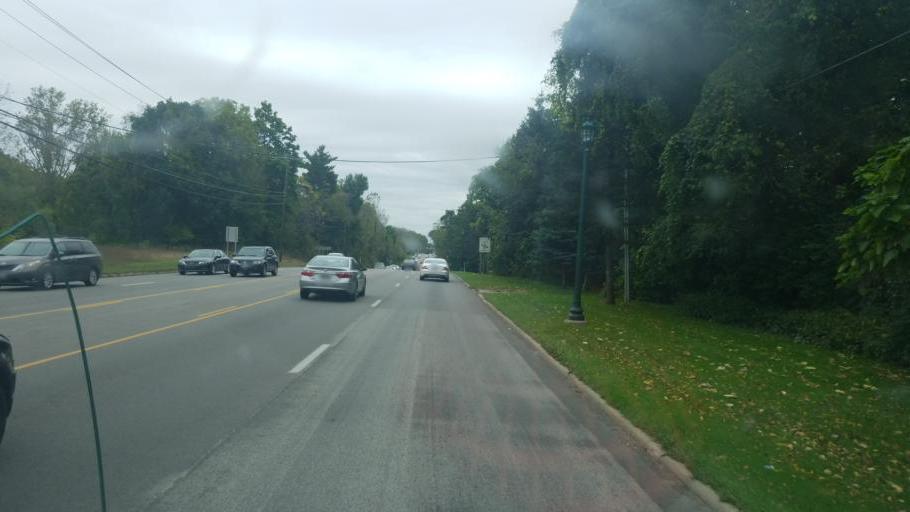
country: US
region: Ohio
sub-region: Lucas County
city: Ottawa Hills
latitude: 41.6768
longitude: -83.6630
